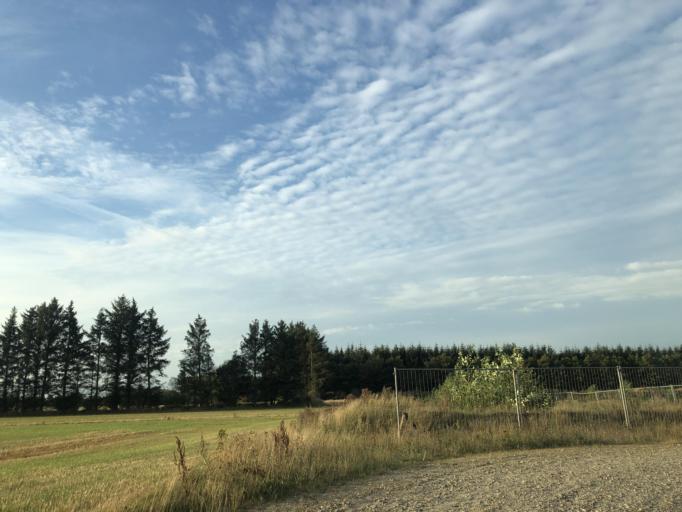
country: DK
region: Central Jutland
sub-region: Holstebro Kommune
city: Ulfborg
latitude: 56.2570
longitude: 8.3209
